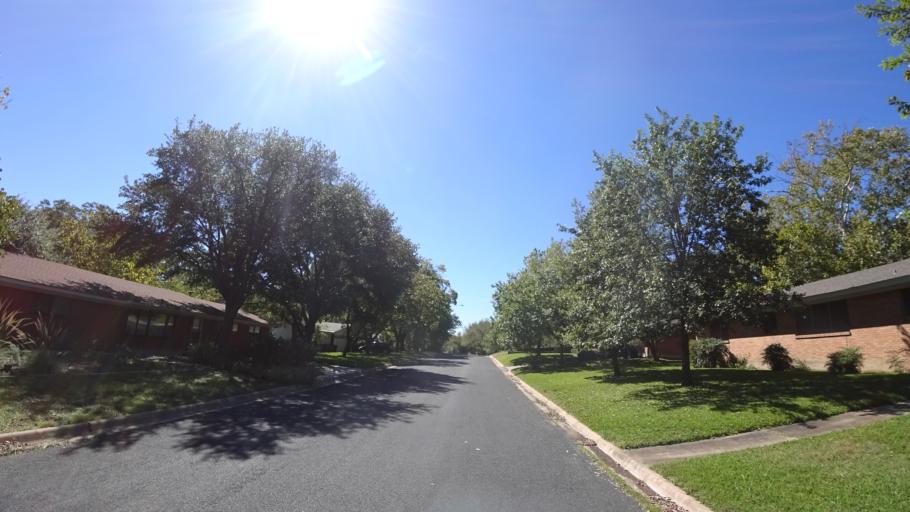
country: US
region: Texas
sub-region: Travis County
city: Austin
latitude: 30.2919
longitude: -97.7093
